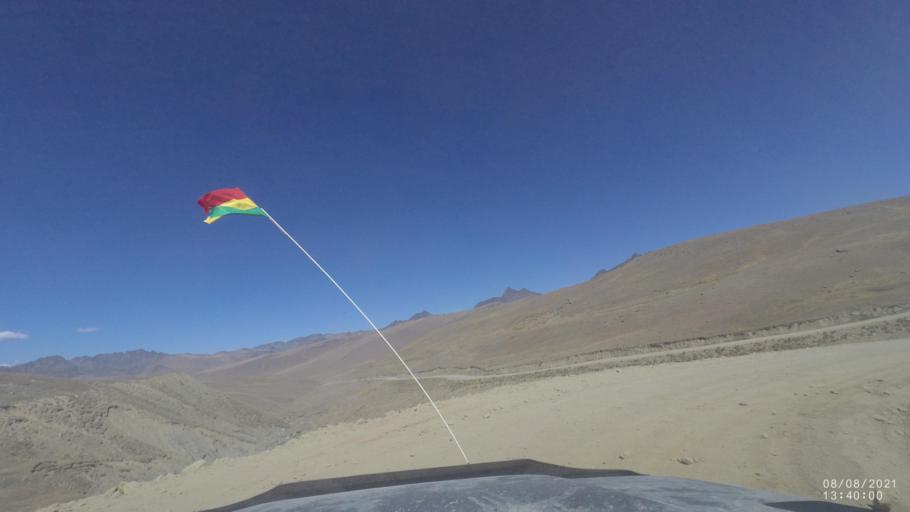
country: BO
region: Cochabamba
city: Colchani
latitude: -17.0868
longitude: -66.4808
